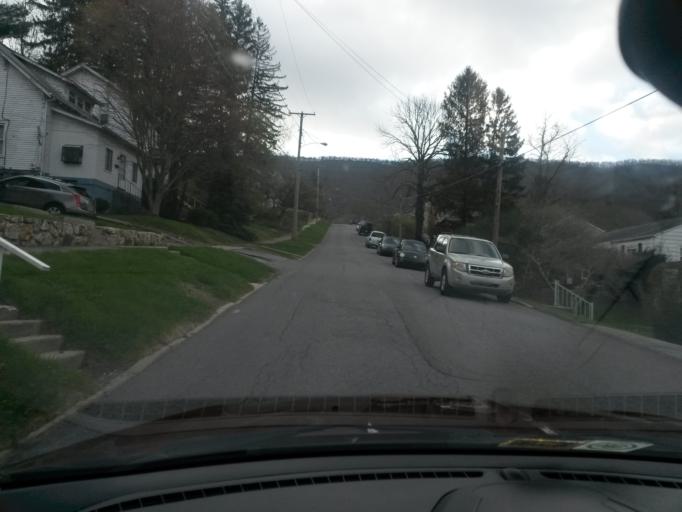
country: US
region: West Virginia
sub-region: Mercer County
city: Bluefield
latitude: 37.2528
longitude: -81.2167
